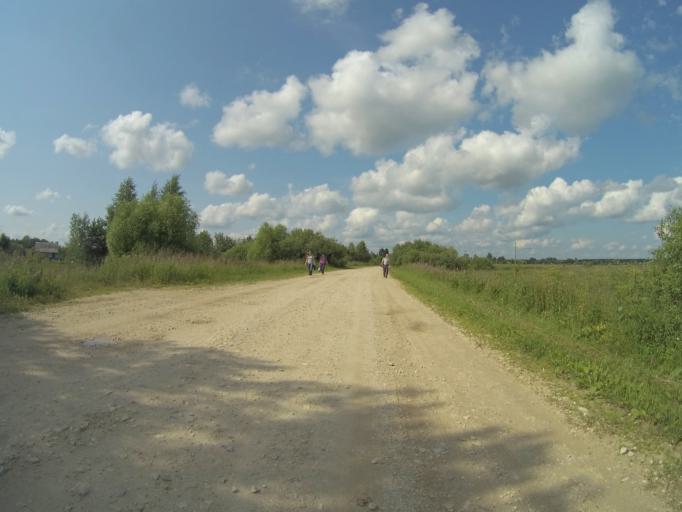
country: RU
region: Vladimir
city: Orgtrud
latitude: 56.2650
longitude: 40.6969
